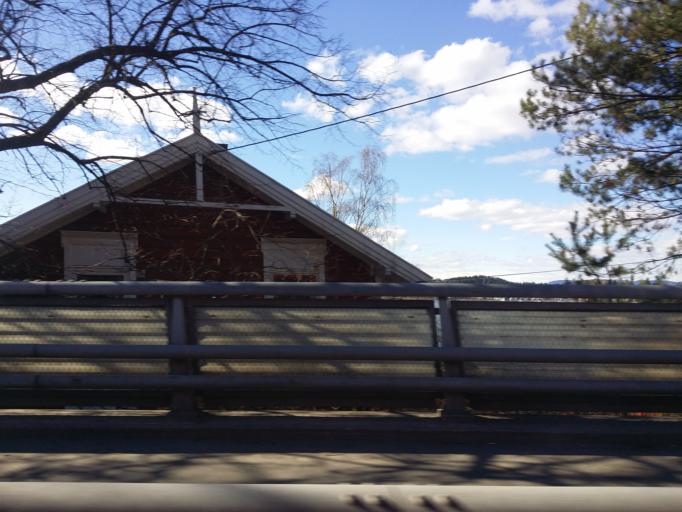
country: NO
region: Akershus
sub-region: Oppegard
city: Kolbotn
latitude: 59.8586
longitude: 10.7844
